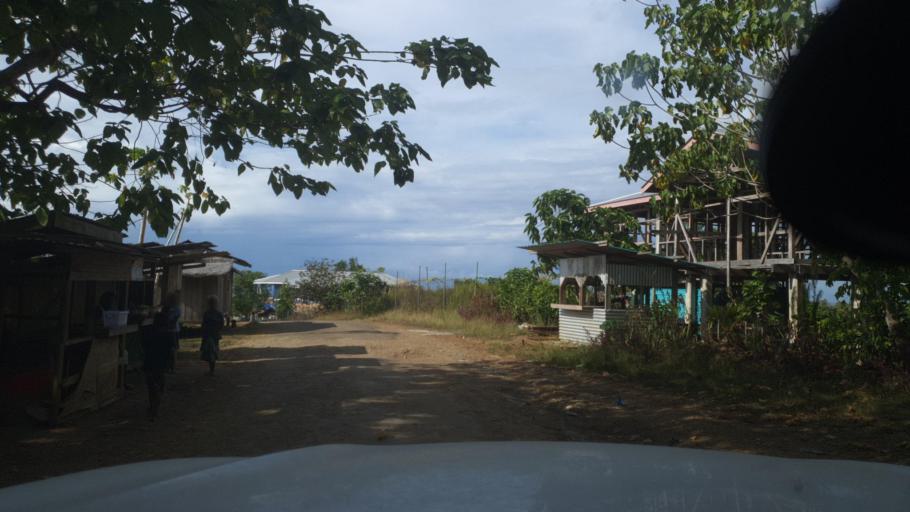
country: SB
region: Guadalcanal
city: Honiara
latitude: -9.4445
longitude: 159.9370
